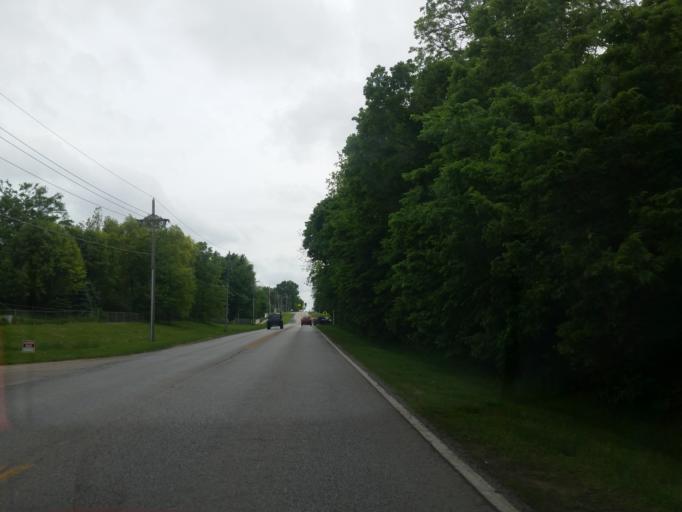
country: US
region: Nebraska
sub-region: Sarpy County
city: Offutt Air Force Base
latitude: 41.1129
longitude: -95.9666
